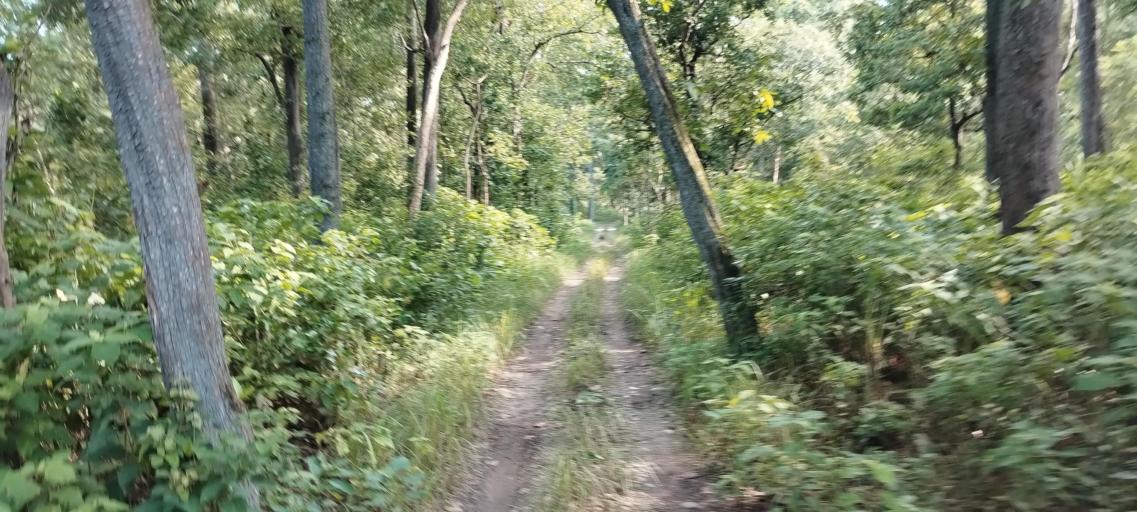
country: NP
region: Far Western
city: Tikapur
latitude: 28.5436
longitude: 81.2866
